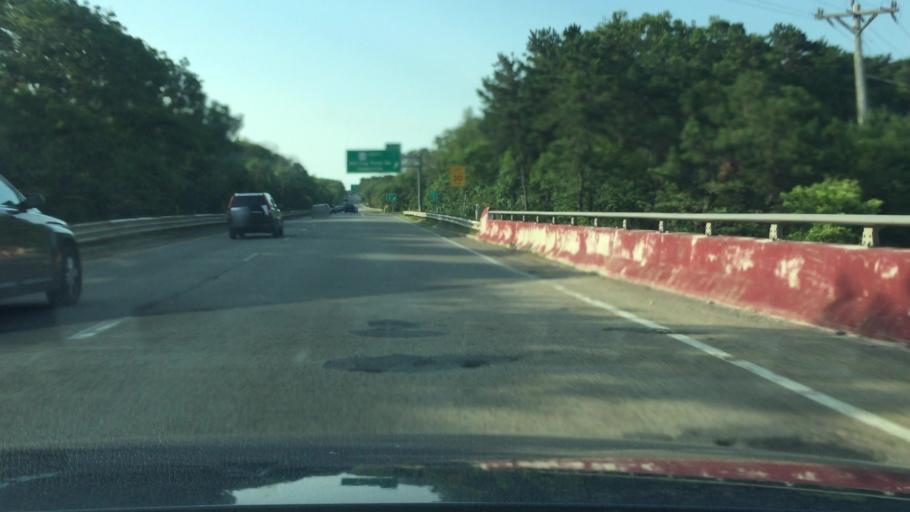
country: US
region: Massachusetts
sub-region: Barnstable County
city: Sagamore
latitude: 41.8134
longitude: -70.5538
